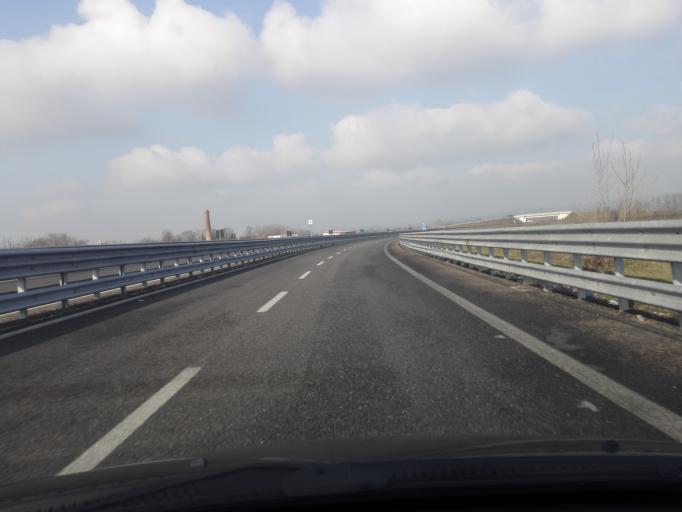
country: IT
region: Piedmont
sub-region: Provincia di Alessandria
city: Alessandria
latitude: 44.9168
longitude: 8.6383
